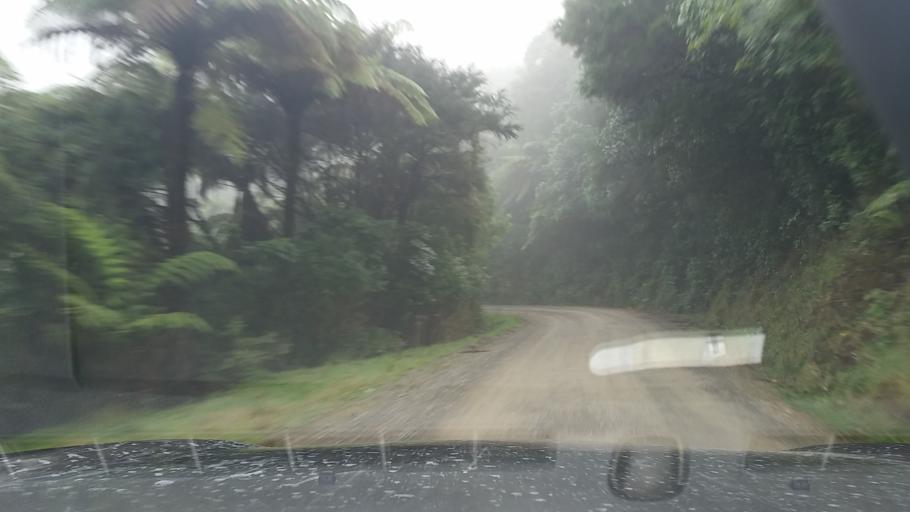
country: NZ
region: Marlborough
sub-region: Marlborough District
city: Picton
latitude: -41.1784
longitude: 173.9825
